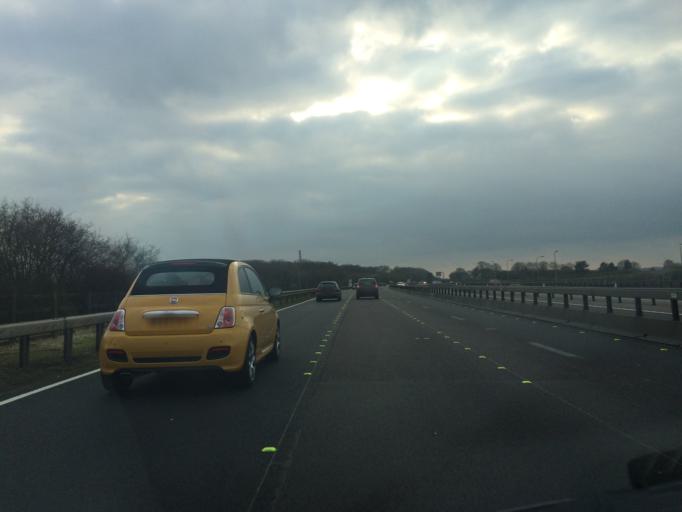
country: GB
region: England
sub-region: West Berkshire
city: Winterbourne
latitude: 51.4527
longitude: -1.3095
